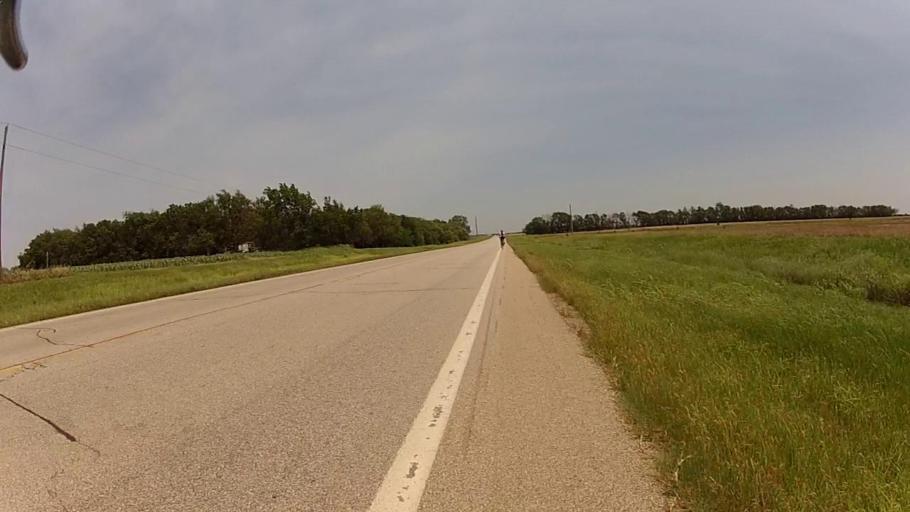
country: US
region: Kansas
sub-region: Cowley County
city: Arkansas City
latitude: 37.0564
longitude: -97.1431
